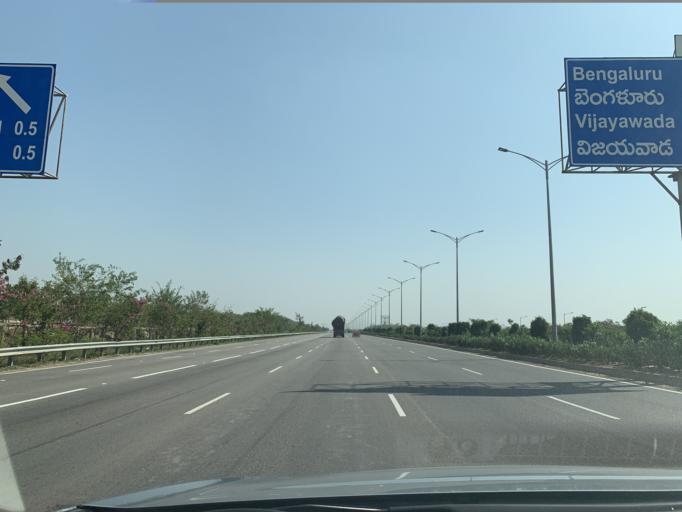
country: IN
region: Telangana
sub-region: Hyderabad
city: Hyderabad
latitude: 17.3600
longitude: 78.3545
